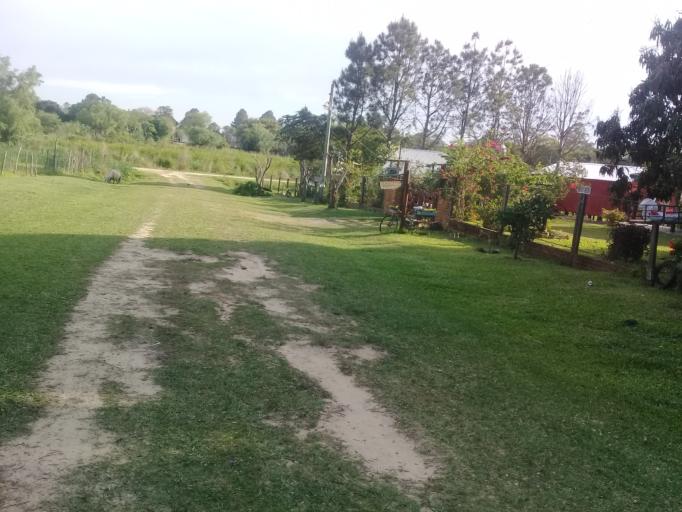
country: AR
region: Corrientes
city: San Luis del Palmar
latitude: -27.4538
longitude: -58.6563
